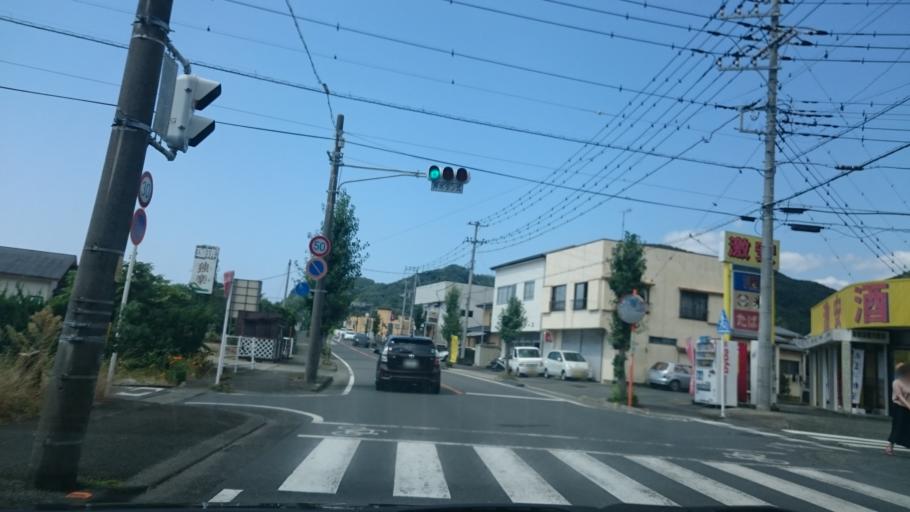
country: JP
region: Shizuoka
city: Shimoda
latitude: 34.7524
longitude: 138.7820
